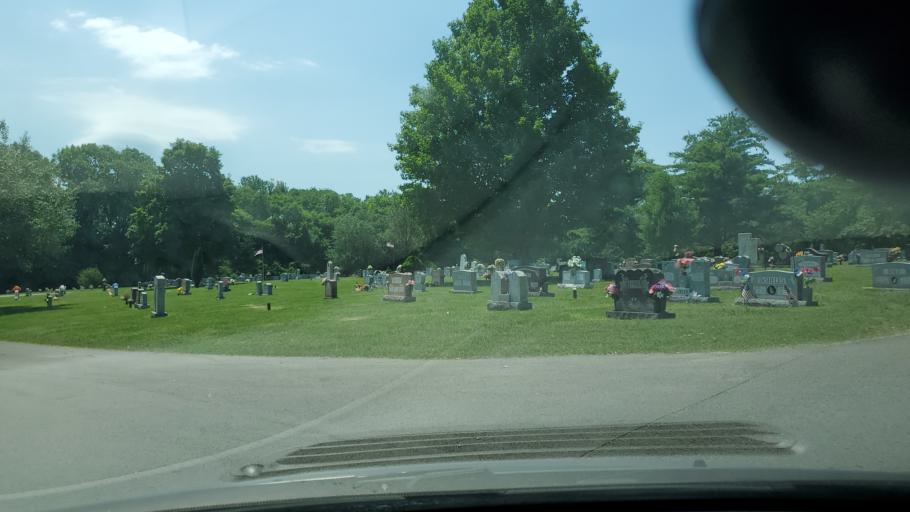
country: US
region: Tennessee
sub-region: Davidson County
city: Lakewood
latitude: 36.2406
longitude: -86.7180
